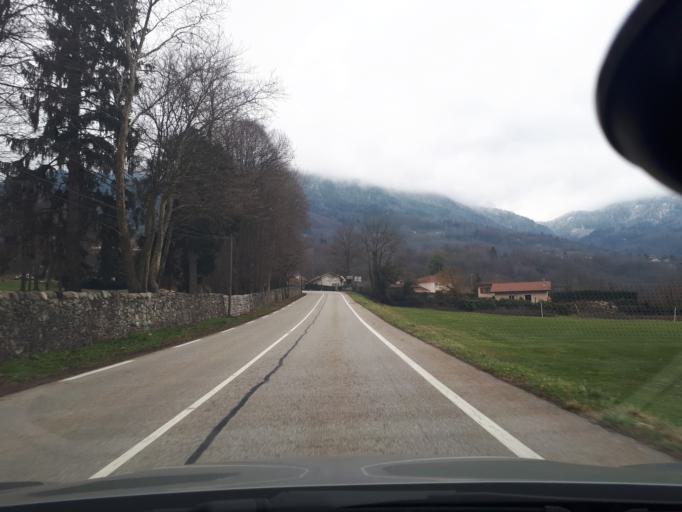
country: FR
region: Rhone-Alpes
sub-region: Departement de l'Isere
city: Vaulnaveys-le-Haut
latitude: 45.1302
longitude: 5.8210
